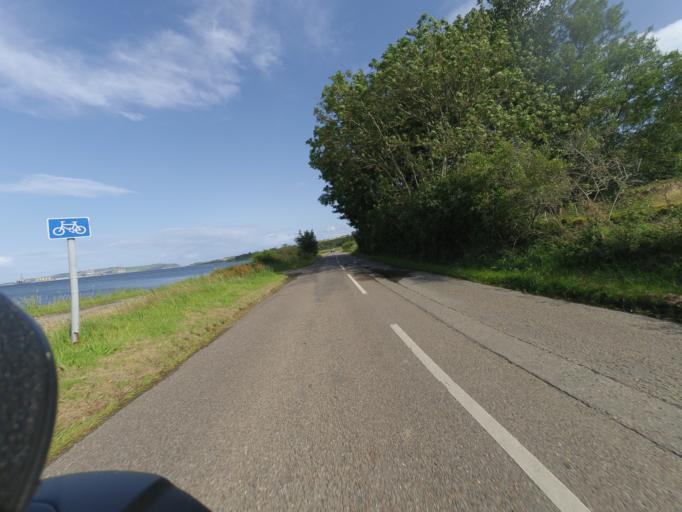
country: GB
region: Scotland
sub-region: Highland
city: Invergordon
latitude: 57.6593
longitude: -4.1325
